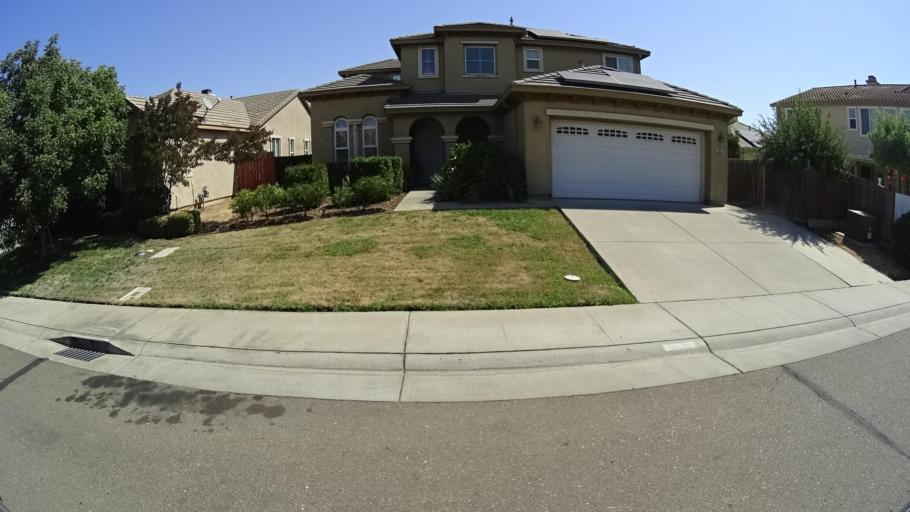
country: US
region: California
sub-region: Sacramento County
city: Laguna
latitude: 38.4431
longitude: -121.3988
